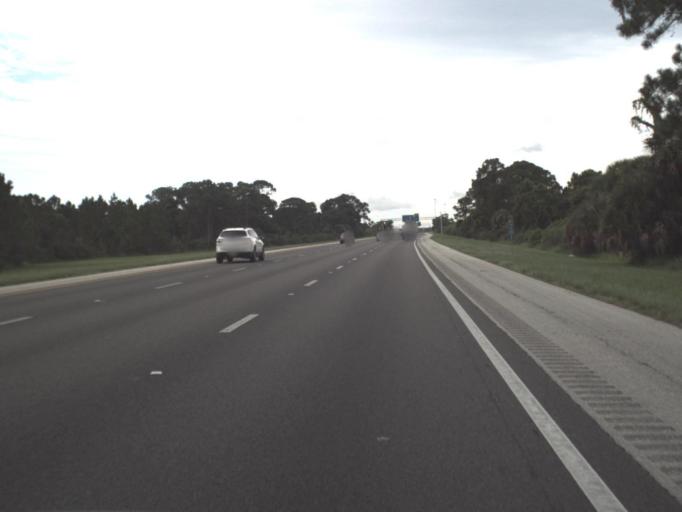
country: US
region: Florida
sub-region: Sarasota County
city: Osprey
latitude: 27.2040
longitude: -82.4423
